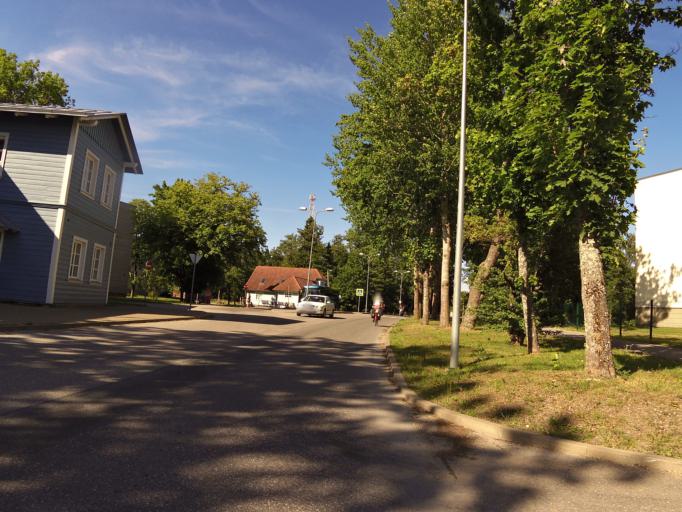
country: EE
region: Hiiumaa
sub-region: Kaerdla linn
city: Kardla
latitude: 59.0009
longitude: 22.7466
